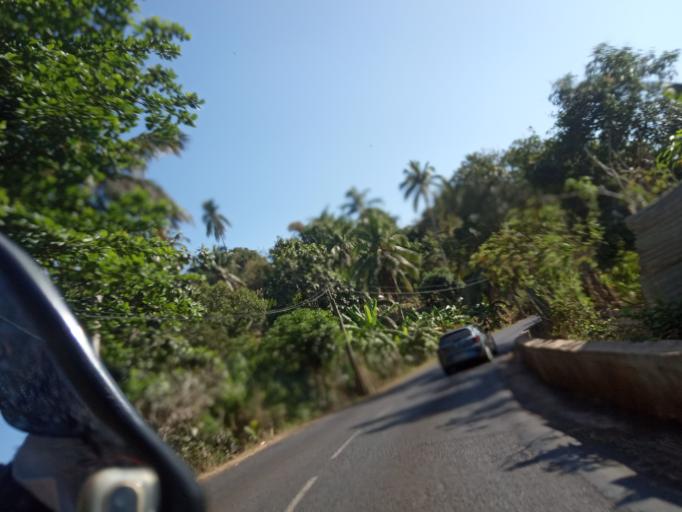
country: YT
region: Bandrele
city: Bandrele
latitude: -12.9033
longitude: 45.1928
